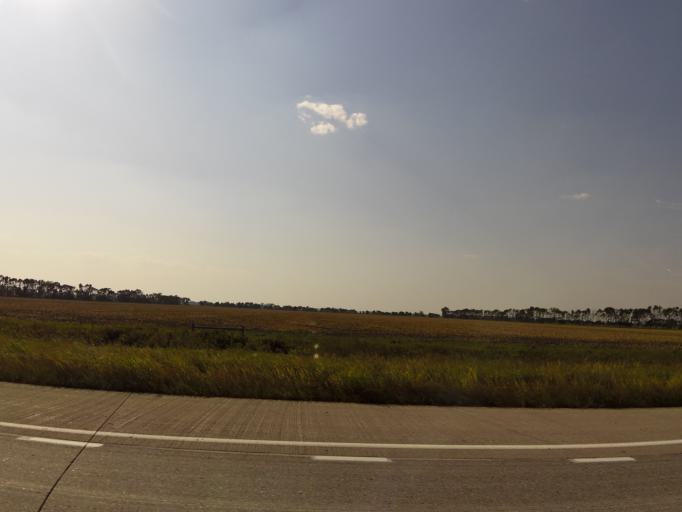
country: US
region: North Dakota
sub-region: Walsh County
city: Grafton
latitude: 48.2316
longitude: -97.1896
